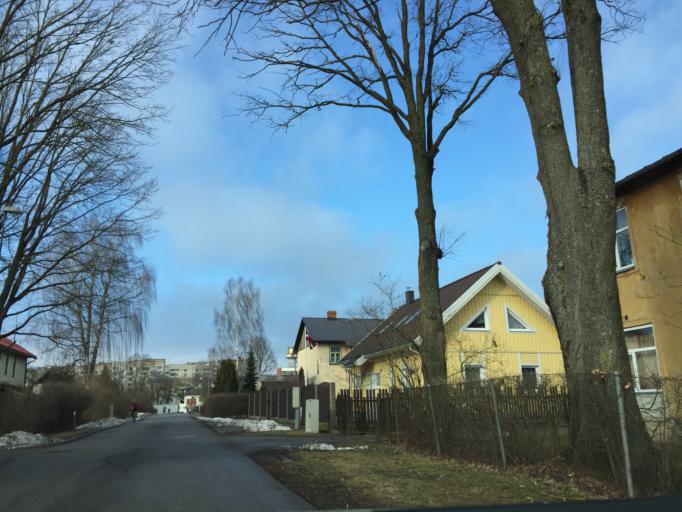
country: LV
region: Lecava
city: Iecava
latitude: 56.5952
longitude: 24.1971
